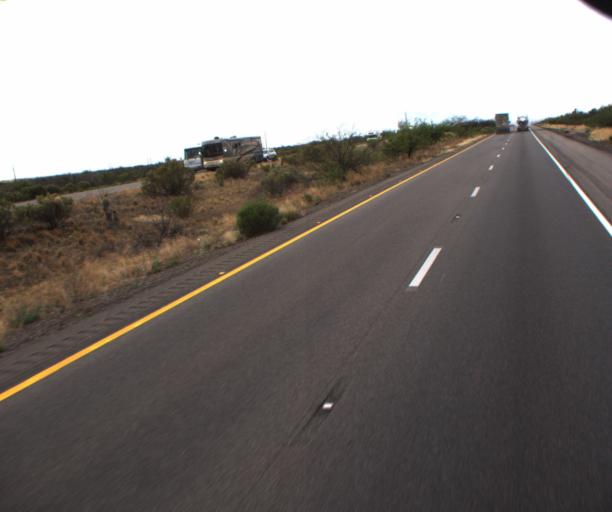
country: US
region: Arizona
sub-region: Cochise County
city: Saint David
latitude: 32.0061
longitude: -110.1400
